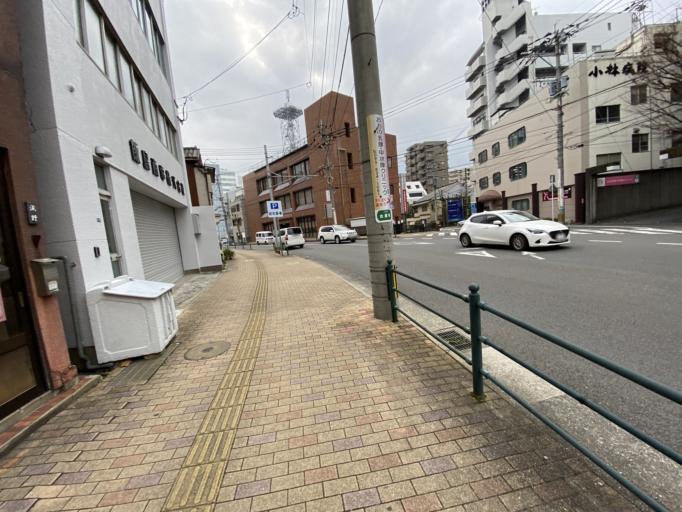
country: JP
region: Nagasaki
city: Nagasaki-shi
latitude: 32.7488
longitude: 129.8743
